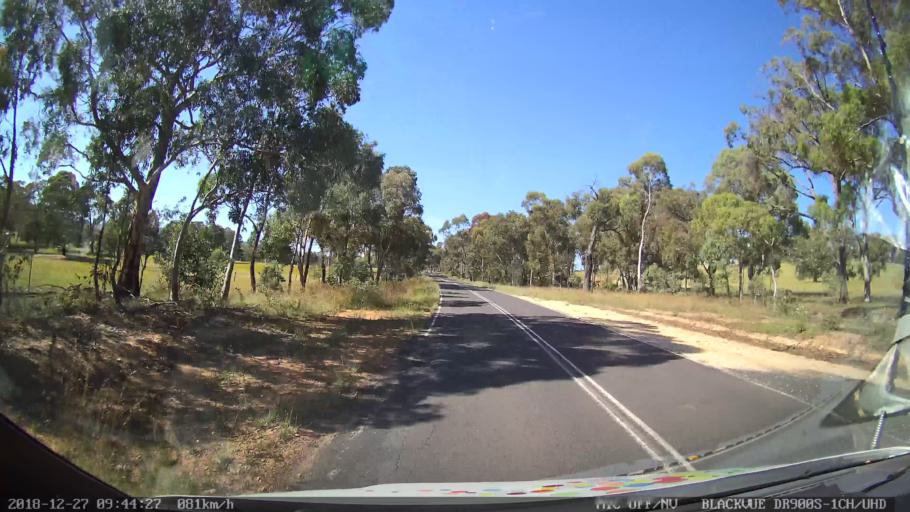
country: AU
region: New South Wales
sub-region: Lithgow
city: Portland
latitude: -33.3155
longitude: 149.9922
